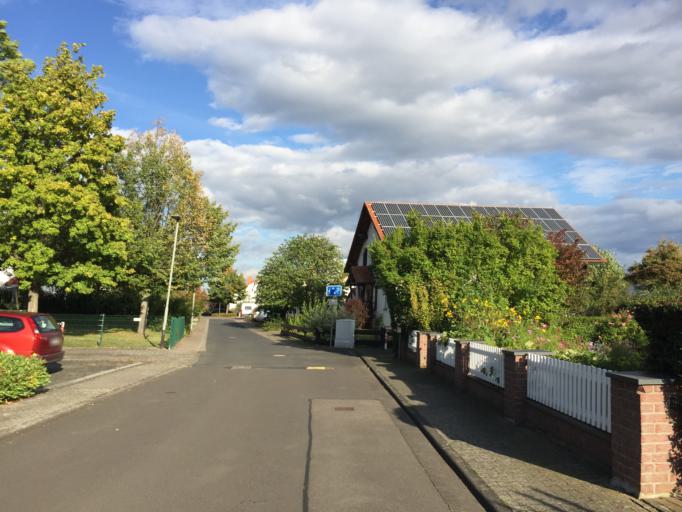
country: DE
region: Hesse
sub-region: Regierungsbezirk Darmstadt
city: Rockenberg
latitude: 50.4625
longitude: 8.7356
